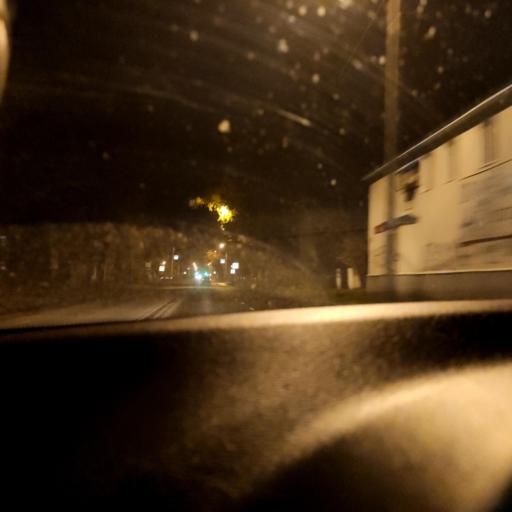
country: RU
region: Samara
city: Samara
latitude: 53.2243
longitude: 50.2600
